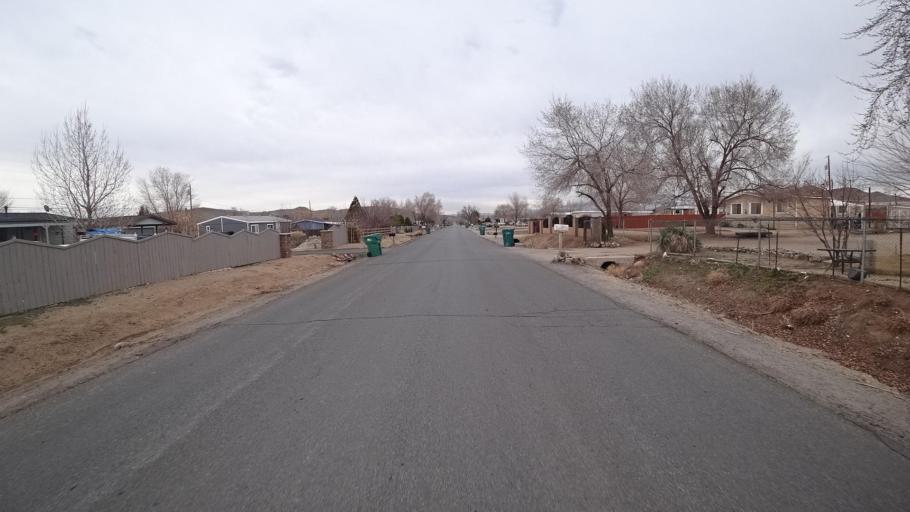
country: US
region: Nevada
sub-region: Washoe County
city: Sun Valley
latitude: 39.6019
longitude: -119.7711
